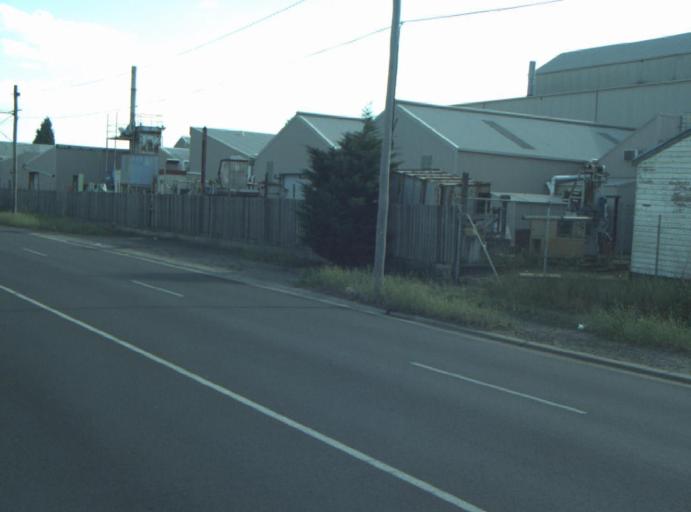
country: AU
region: Victoria
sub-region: Greater Geelong
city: Bell Park
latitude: -38.1200
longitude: 144.3481
